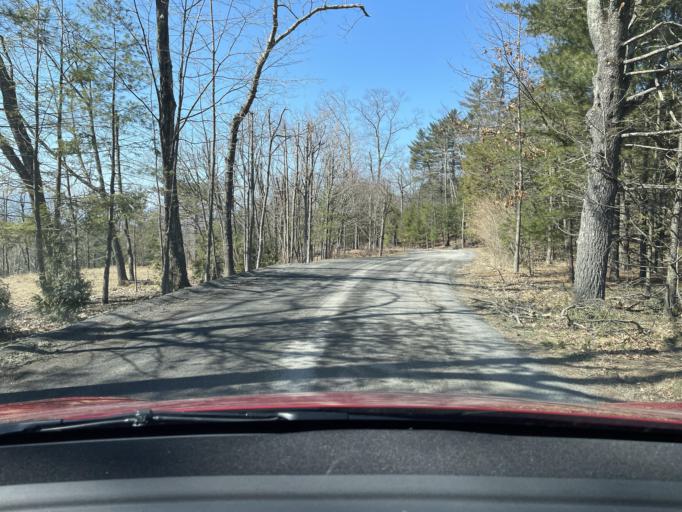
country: US
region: New York
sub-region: Ulster County
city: West Hurley
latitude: 42.0113
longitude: -74.1347
